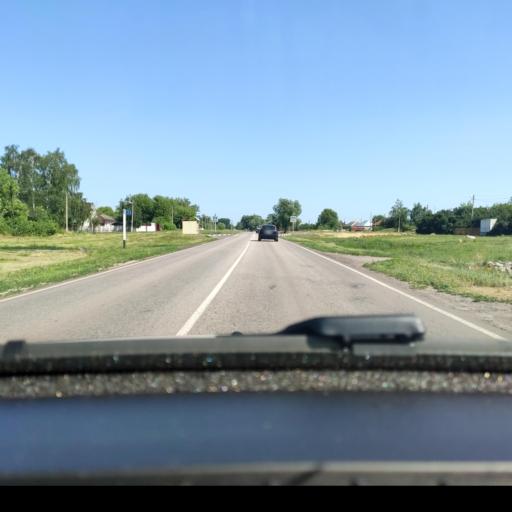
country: RU
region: Voronezj
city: Verkhnyaya Khava
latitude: 51.6719
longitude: 39.9532
